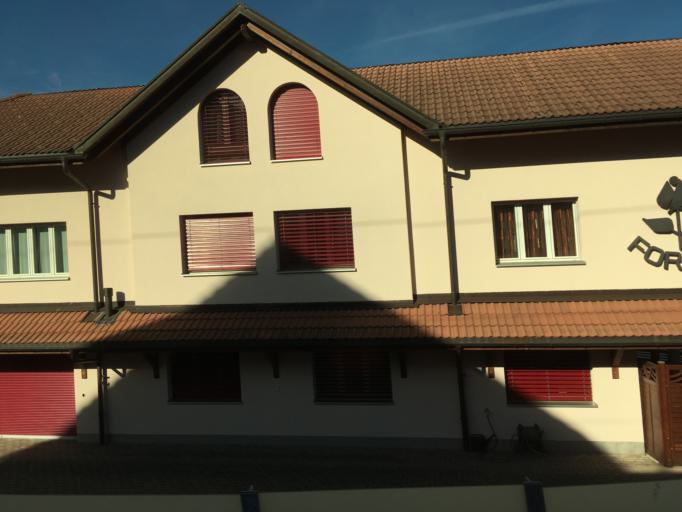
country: CH
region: Schwyz
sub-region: Bezirk Hoefe
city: Wollerau
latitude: 47.1965
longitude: 8.7194
